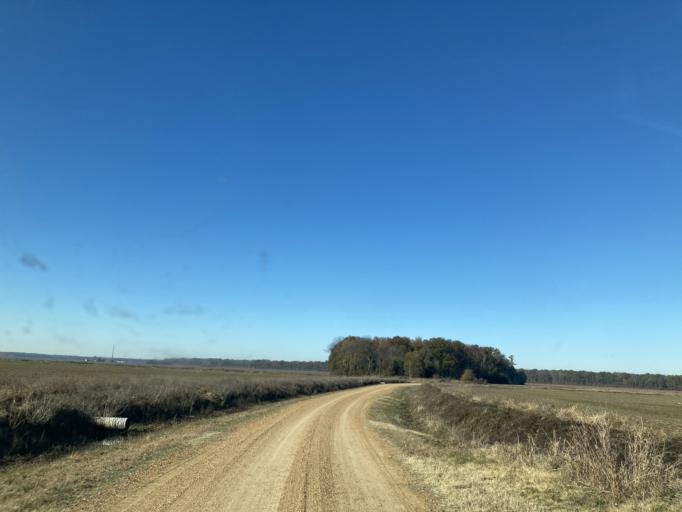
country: US
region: Mississippi
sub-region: Sharkey County
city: Rolling Fork
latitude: 32.9008
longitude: -90.6617
